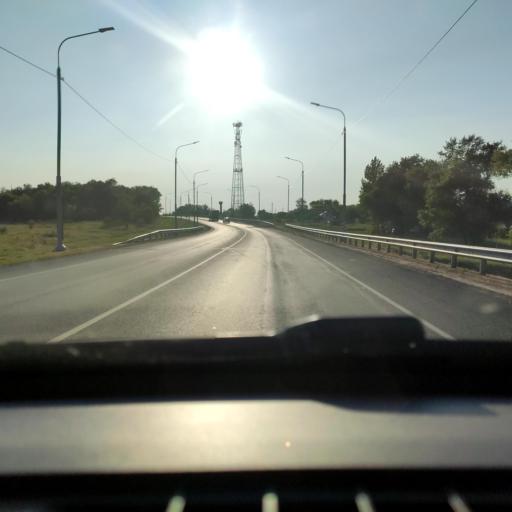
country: RU
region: Voronezj
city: Kashirskoye
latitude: 51.5005
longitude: 39.5796
